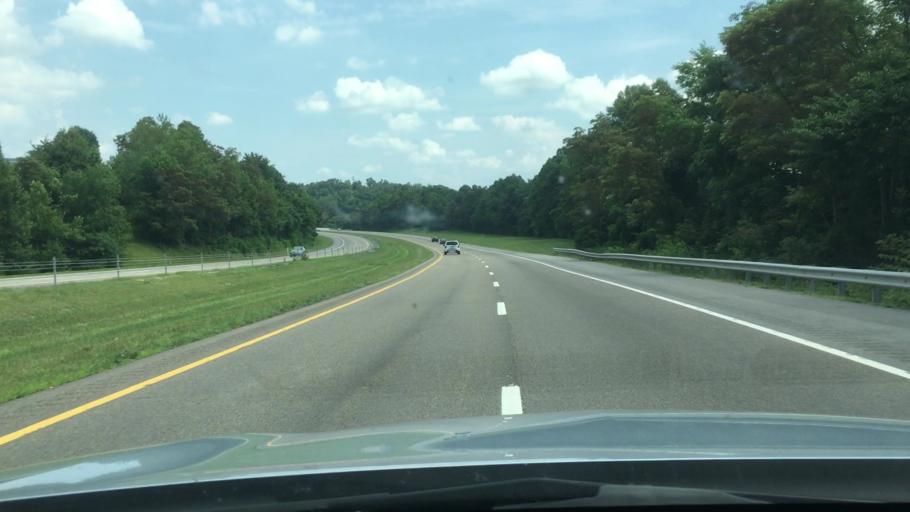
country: US
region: Tennessee
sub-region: Unicoi County
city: Unicoi
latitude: 36.2357
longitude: -82.3303
